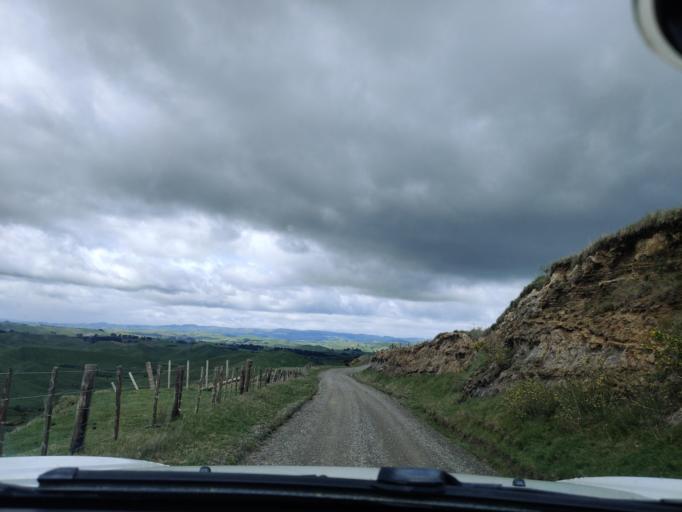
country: NZ
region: Manawatu-Wanganui
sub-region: Palmerston North City
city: Palmerston North
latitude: -40.2844
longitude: 175.8607
